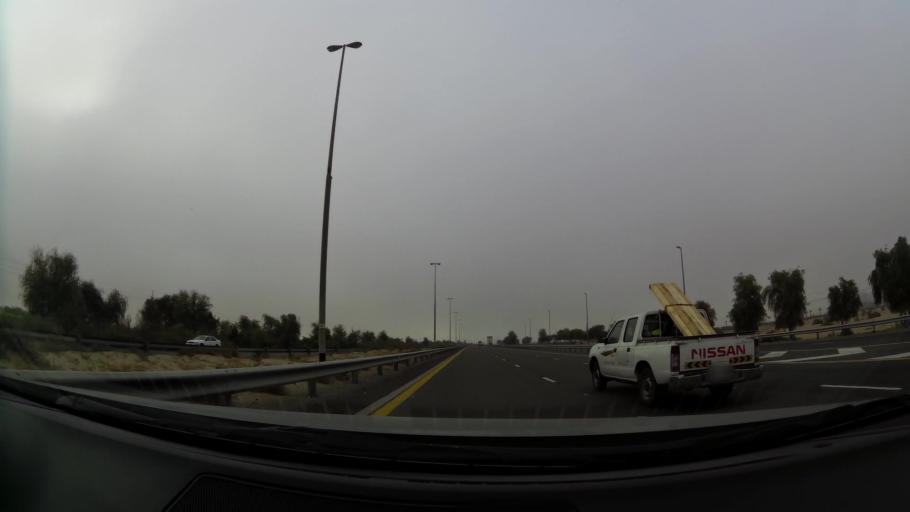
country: AE
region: Dubai
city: Dubai
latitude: 25.0532
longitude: 55.4238
